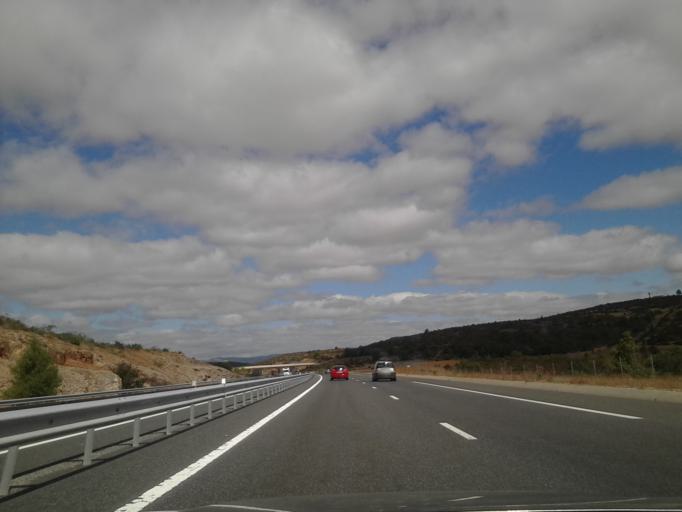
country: FR
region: Midi-Pyrenees
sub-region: Departement de l'Aveyron
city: Creissels
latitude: 44.0489
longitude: 3.0514
